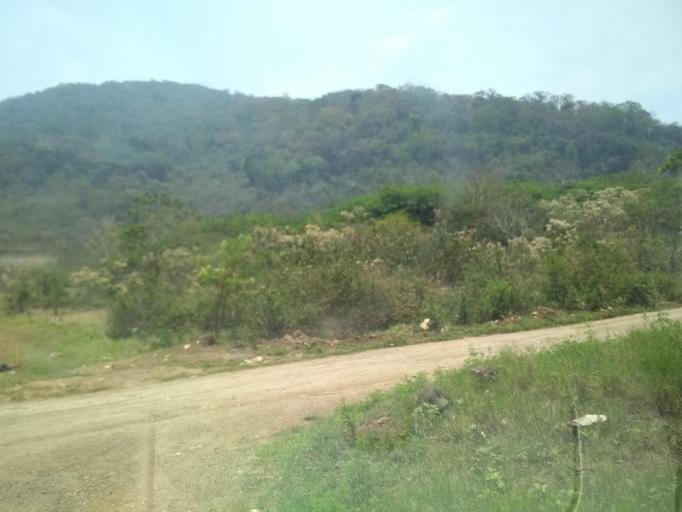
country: MX
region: Veracruz
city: Cosolapa
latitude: 18.5916
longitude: -96.6978
